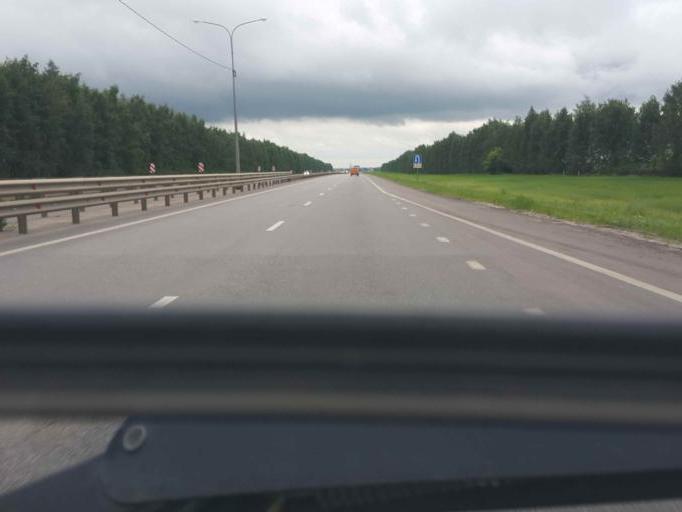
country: RU
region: Tambov
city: Zavoronezhskoye
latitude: 52.8488
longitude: 40.8077
